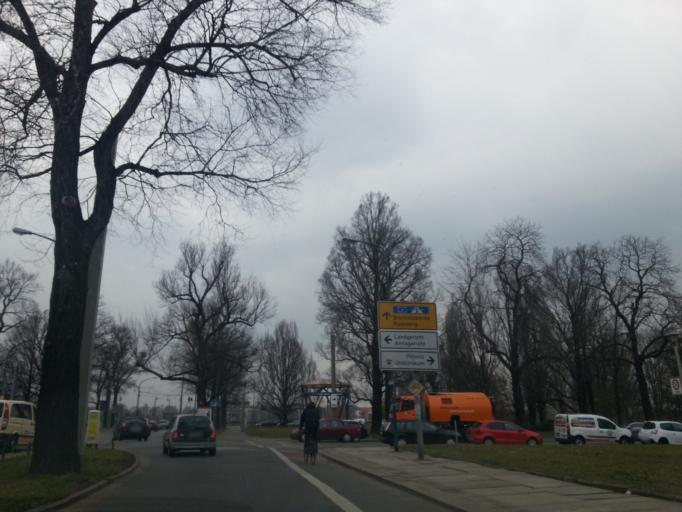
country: DE
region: Saxony
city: Dresden
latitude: 51.0550
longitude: 13.7572
